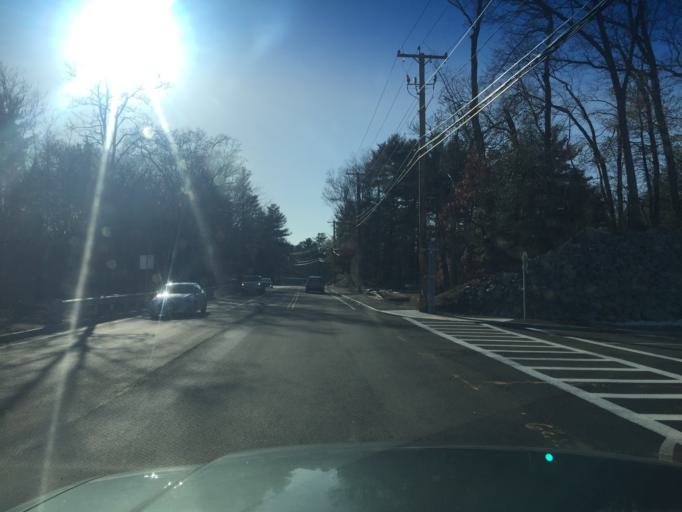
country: US
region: Massachusetts
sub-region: Norfolk County
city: Bellingham
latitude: 42.0821
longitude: -71.4606
